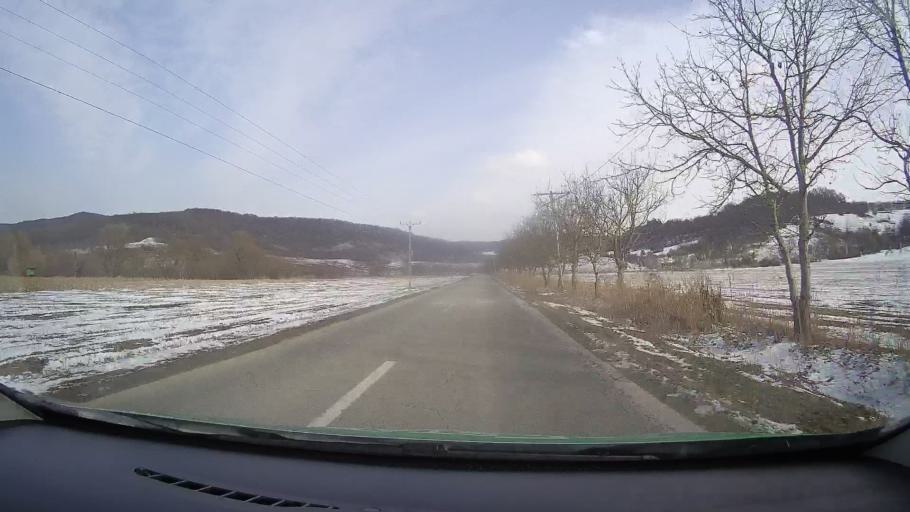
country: RO
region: Mures
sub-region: Comuna Apold
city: Apold
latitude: 46.1422
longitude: 24.8060
